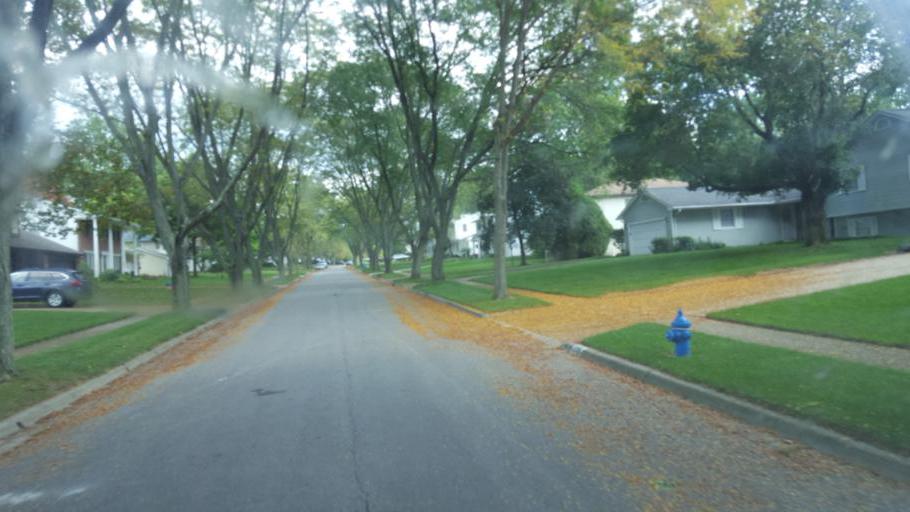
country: US
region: Ohio
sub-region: Franklin County
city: Worthington
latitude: 40.0969
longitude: -83.0266
